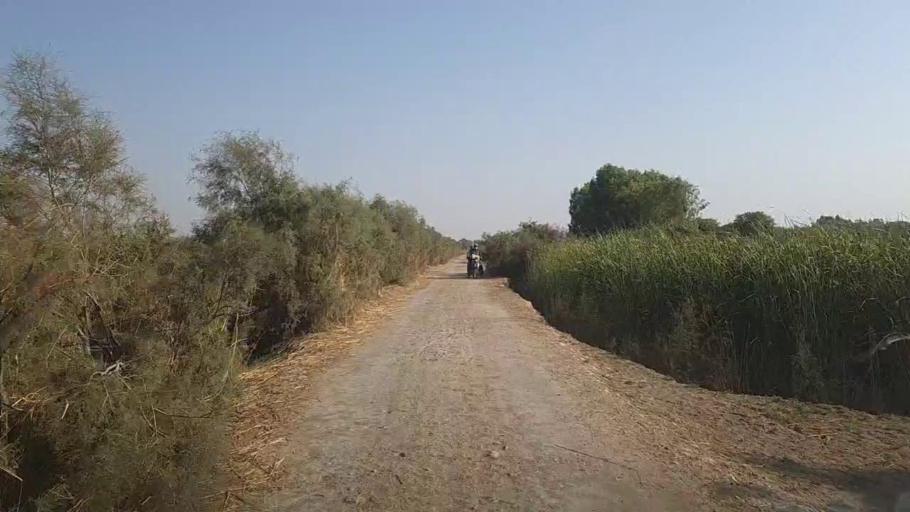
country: PK
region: Sindh
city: Kandhkot
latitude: 28.3563
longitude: 69.3342
